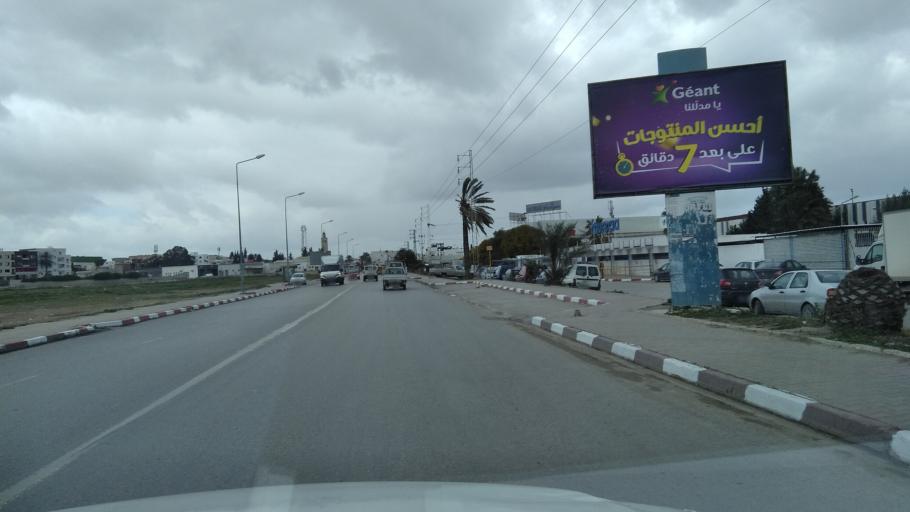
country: TN
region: Bin 'Arus
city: Ben Arous
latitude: 36.7487
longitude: 10.2288
